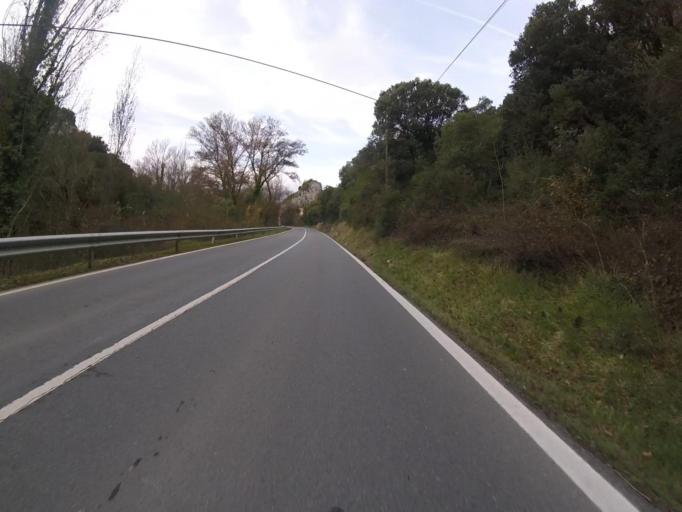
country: ES
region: Navarre
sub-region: Provincia de Navarra
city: Estella
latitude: 42.7009
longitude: -2.0572
